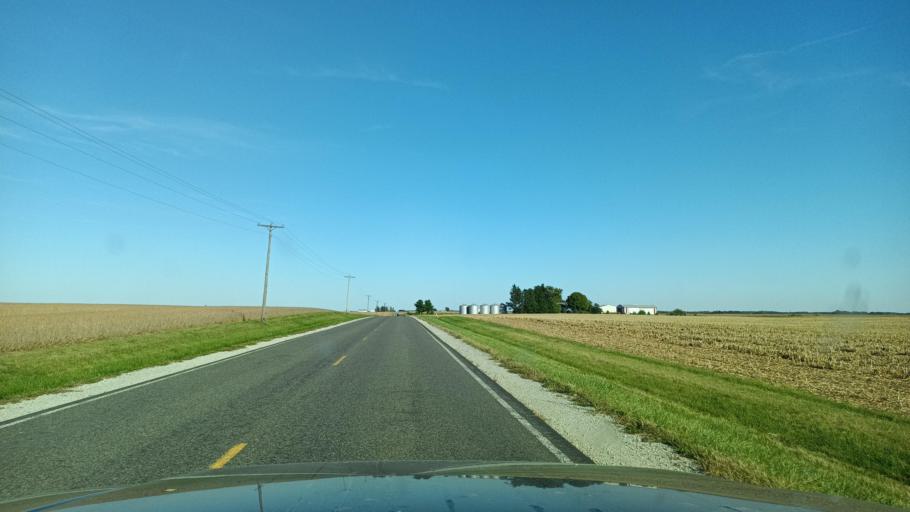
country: US
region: Illinois
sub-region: De Witt County
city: Clinton
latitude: 40.2244
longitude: -88.8946
